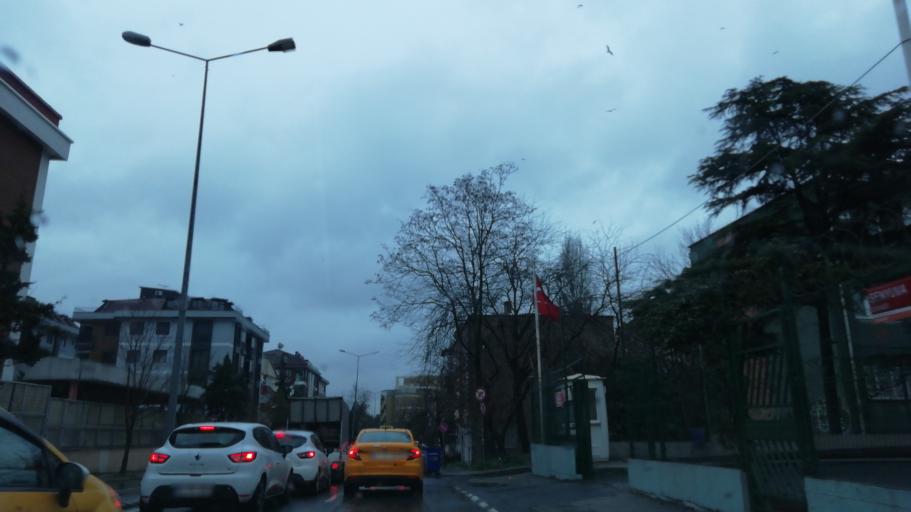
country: TR
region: Istanbul
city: Bahcelievler
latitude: 40.9956
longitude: 28.8671
